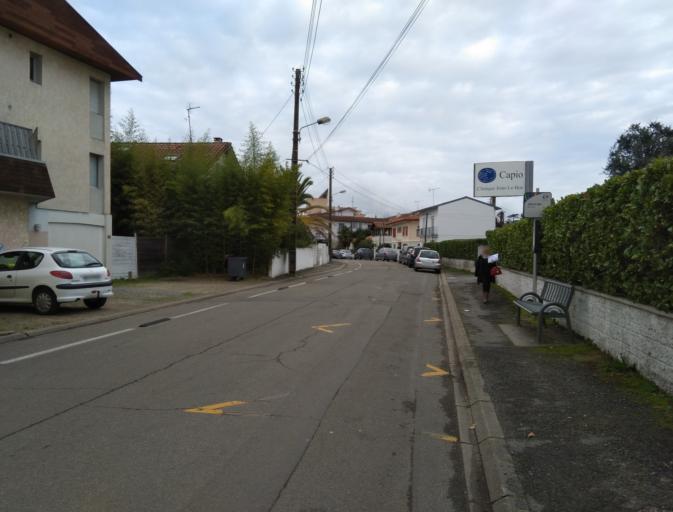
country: FR
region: Aquitaine
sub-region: Departement des Landes
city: Dax
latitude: 43.7023
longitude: -1.0595
